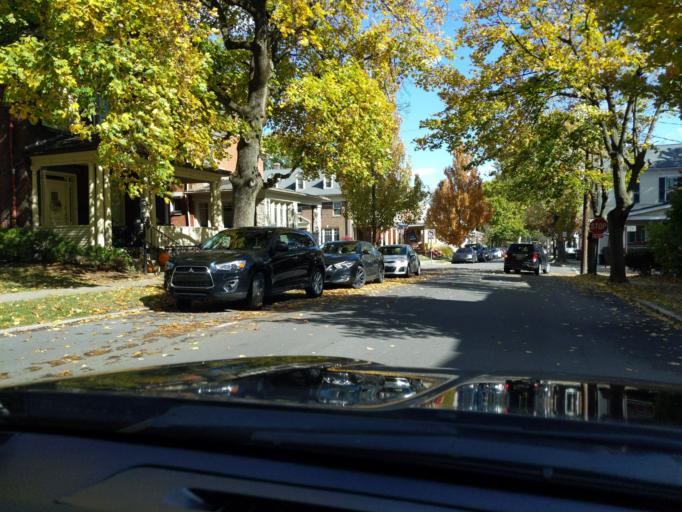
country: US
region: Pennsylvania
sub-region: Blair County
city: Hollidaysburg
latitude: 40.4304
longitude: -78.3944
